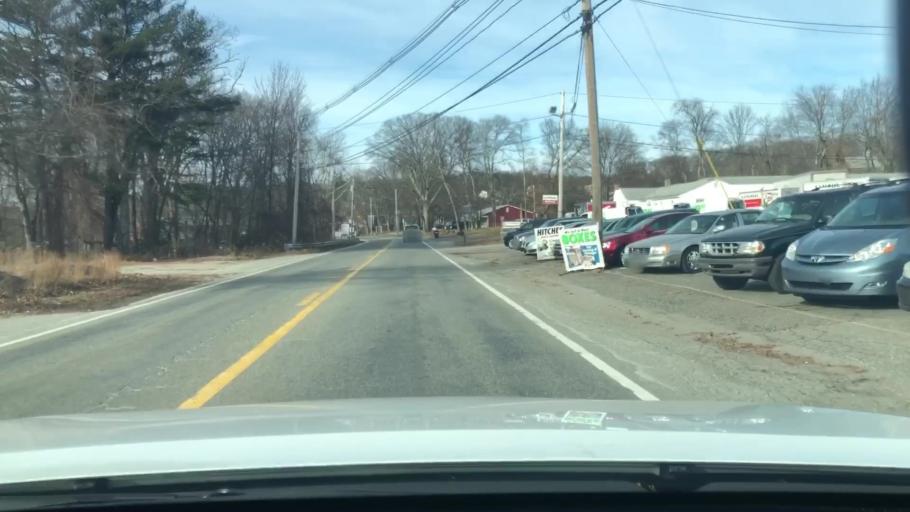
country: US
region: Massachusetts
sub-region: Worcester County
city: Upton
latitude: 42.1606
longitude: -71.5834
